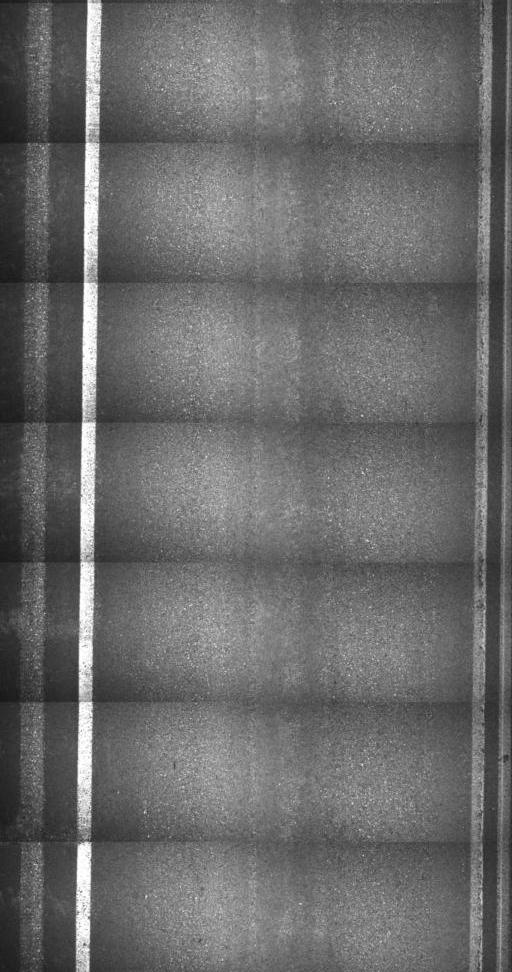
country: CA
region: Quebec
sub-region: Monteregie
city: Sutton
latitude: 44.9684
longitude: -72.4423
